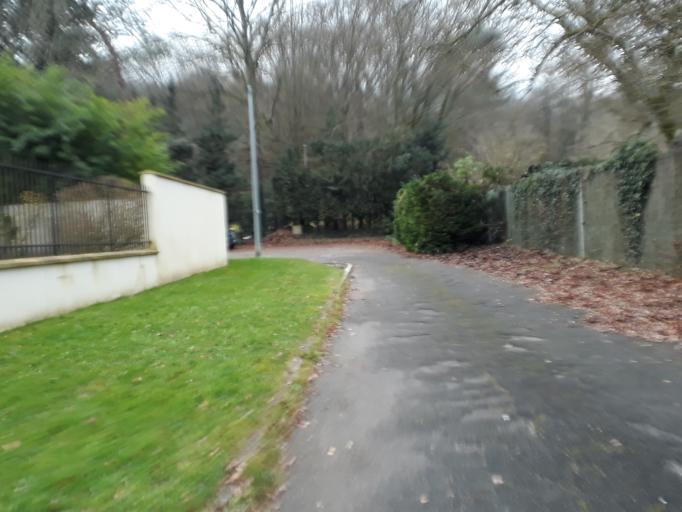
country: FR
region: Ile-de-France
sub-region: Departement de Seine-et-Marne
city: Chartrettes
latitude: 48.4800
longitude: 2.6742
